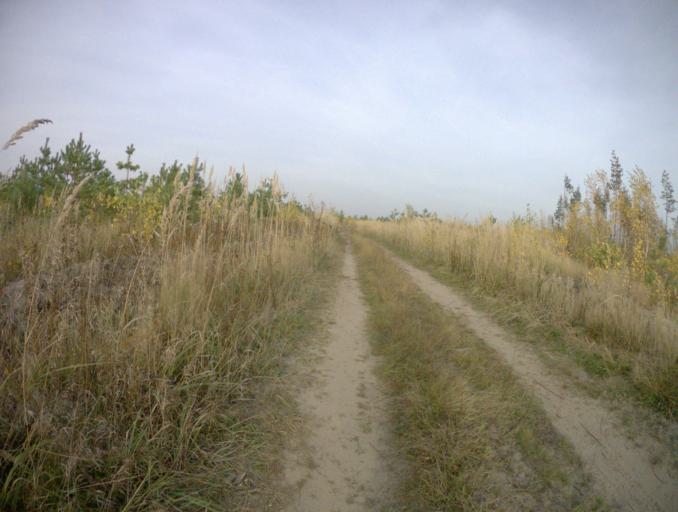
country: RU
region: Vladimir
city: Sobinka
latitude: 55.9715
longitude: 40.0576
